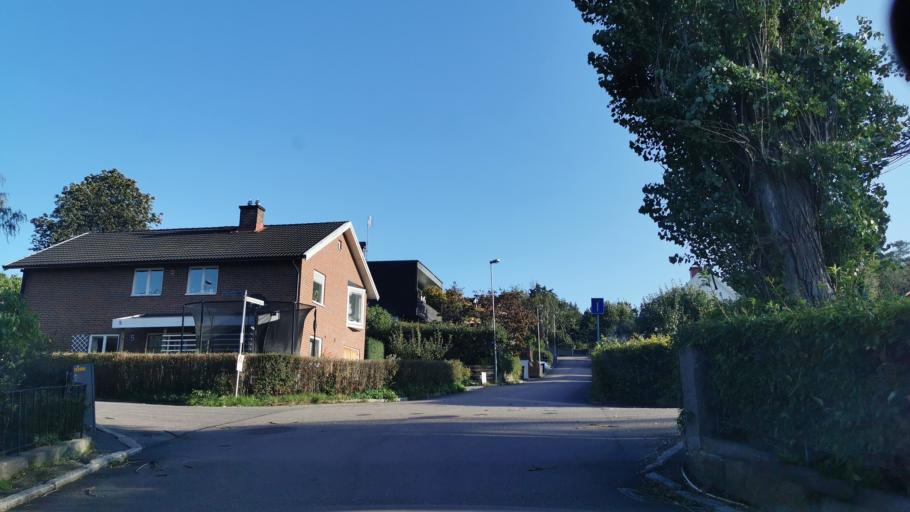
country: SE
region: Vaestra Goetaland
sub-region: Partille Kommun
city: Partille
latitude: 57.7262
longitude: 12.0609
